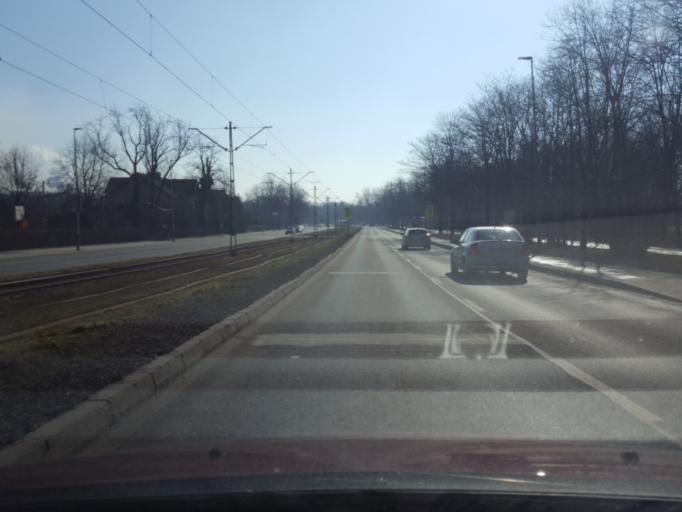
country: PL
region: Lesser Poland Voivodeship
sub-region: Powiat wielicki
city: Kokotow
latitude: 50.0681
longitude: 20.0537
